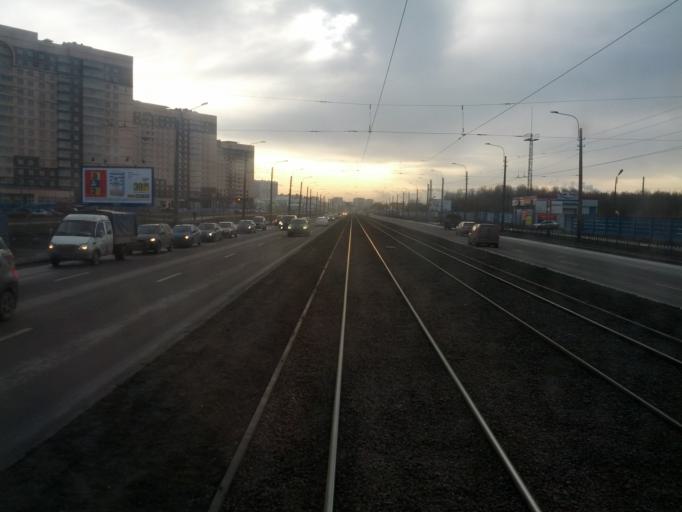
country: RU
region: St.-Petersburg
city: Centralniy
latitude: 59.9173
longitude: 30.4278
